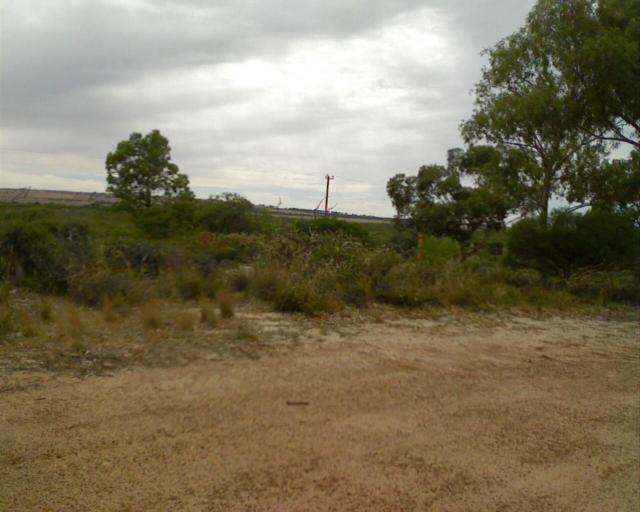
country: AU
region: Western Australia
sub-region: Dandaragan
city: Jurien Bay
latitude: -29.8251
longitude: 115.2668
